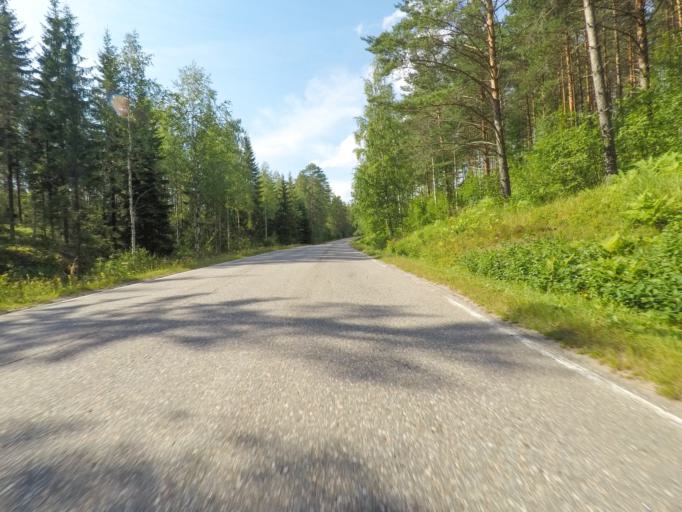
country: FI
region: Southern Savonia
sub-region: Mikkeli
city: Puumala
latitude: 61.6732
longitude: 28.2292
